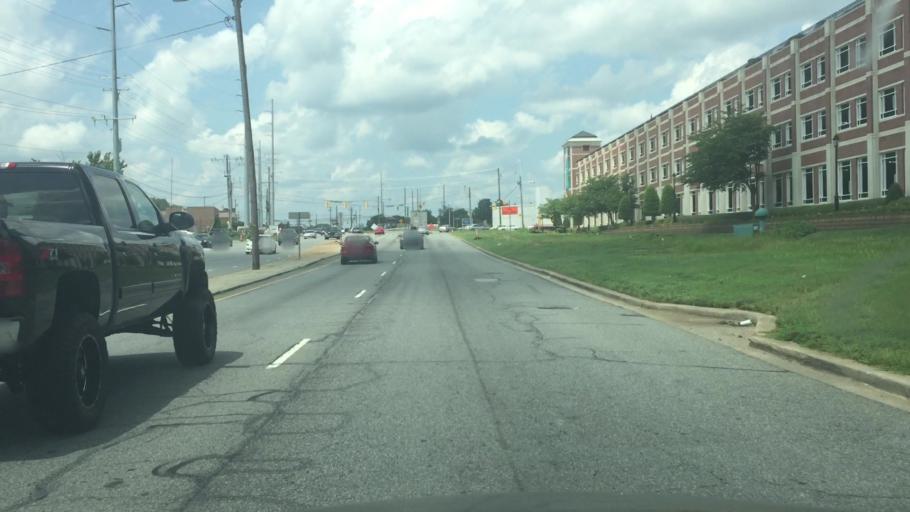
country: US
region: North Carolina
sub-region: Cabarrus County
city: Concord
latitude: 35.4364
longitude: -80.6041
